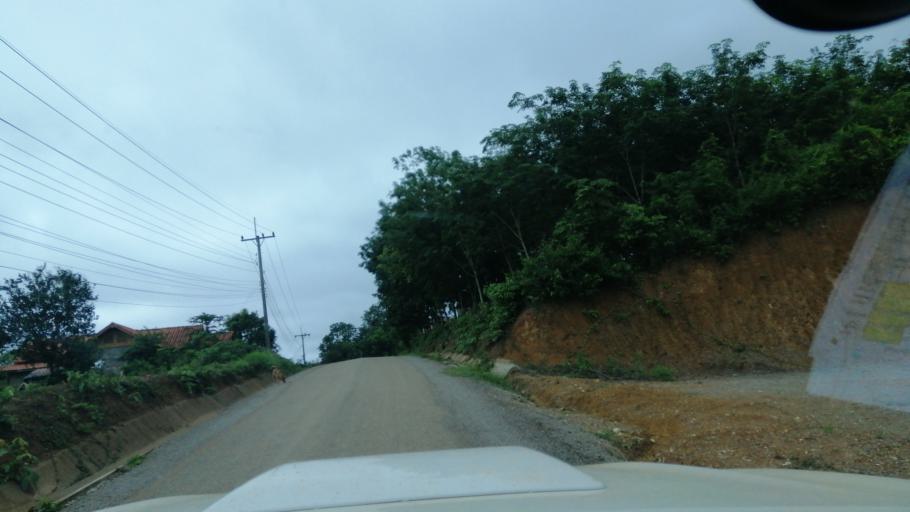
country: LA
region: Xiagnabouli
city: Muang Kenthao
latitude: 17.9519
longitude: 101.4060
